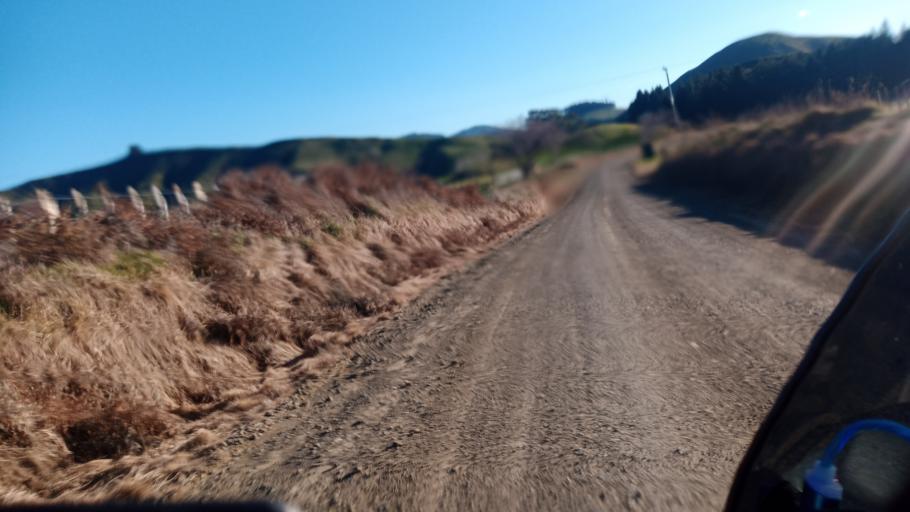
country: NZ
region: Bay of Plenty
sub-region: Opotiki District
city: Opotiki
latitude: -38.4588
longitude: 177.4290
